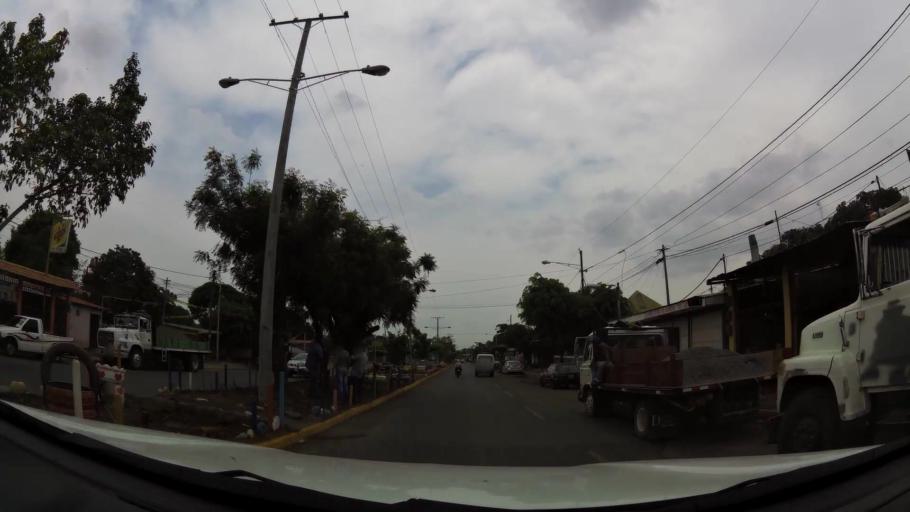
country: NI
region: Managua
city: Managua
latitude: 12.1251
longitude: -86.2175
